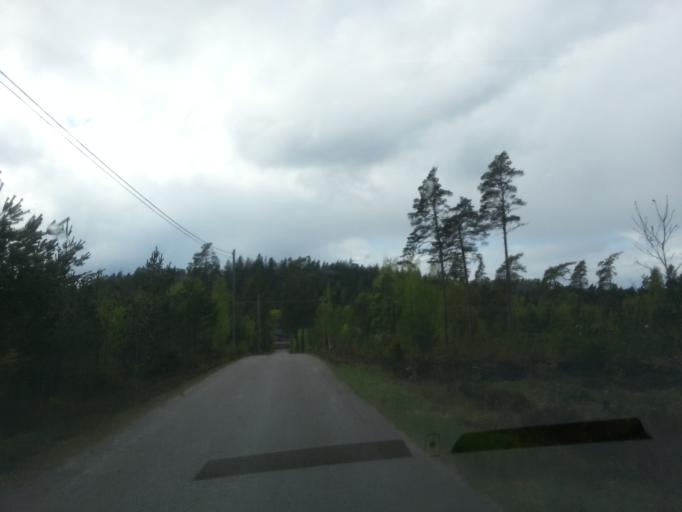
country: SE
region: OEstergoetland
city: Lindo
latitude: 58.6903
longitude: 16.2596
